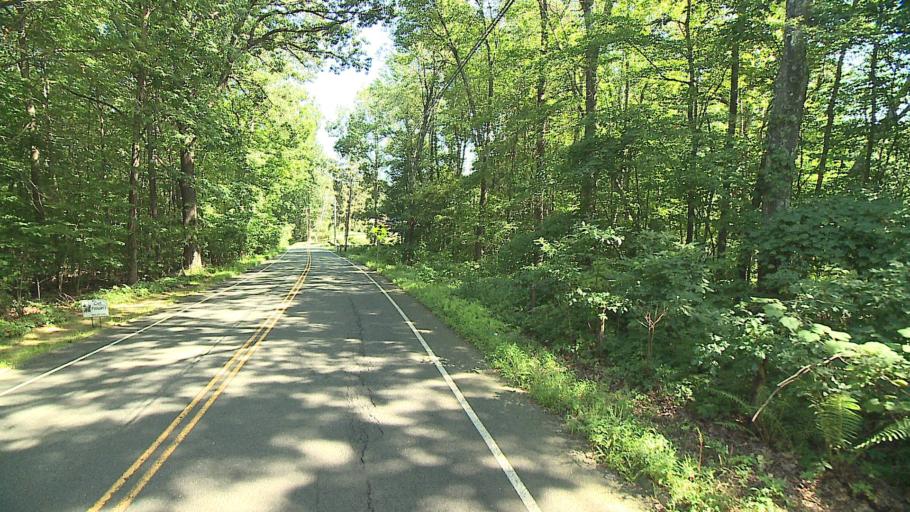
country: US
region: Connecticut
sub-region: Hartford County
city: West Simsbury
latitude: 41.8841
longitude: -72.8748
